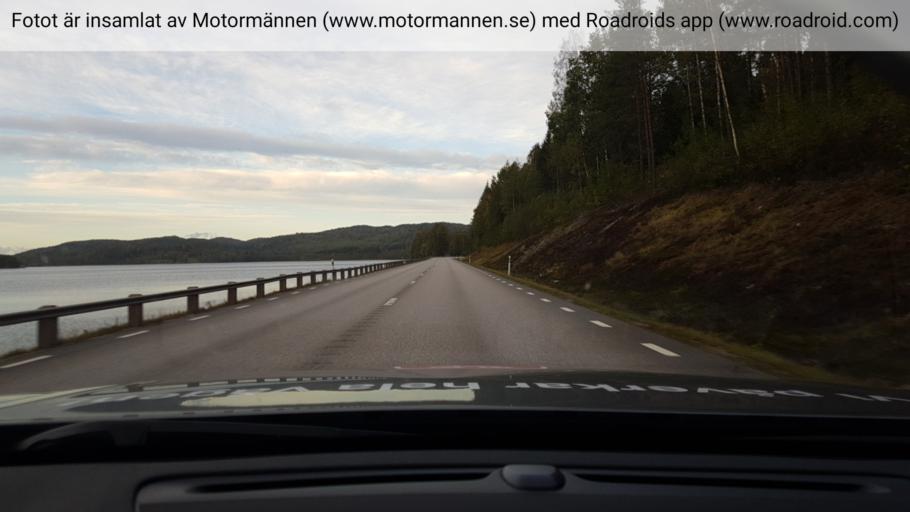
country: SE
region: Vaestra Goetaland
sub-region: Bengtsfors Kommun
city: Dals Langed
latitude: 59.0558
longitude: 12.4394
